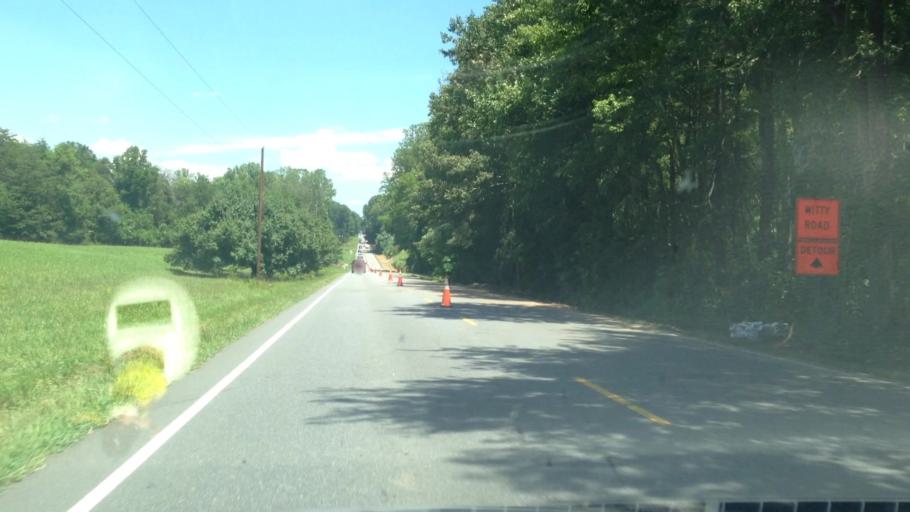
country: US
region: North Carolina
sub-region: Guilford County
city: Summerfield
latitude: 36.2636
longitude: -79.8616
